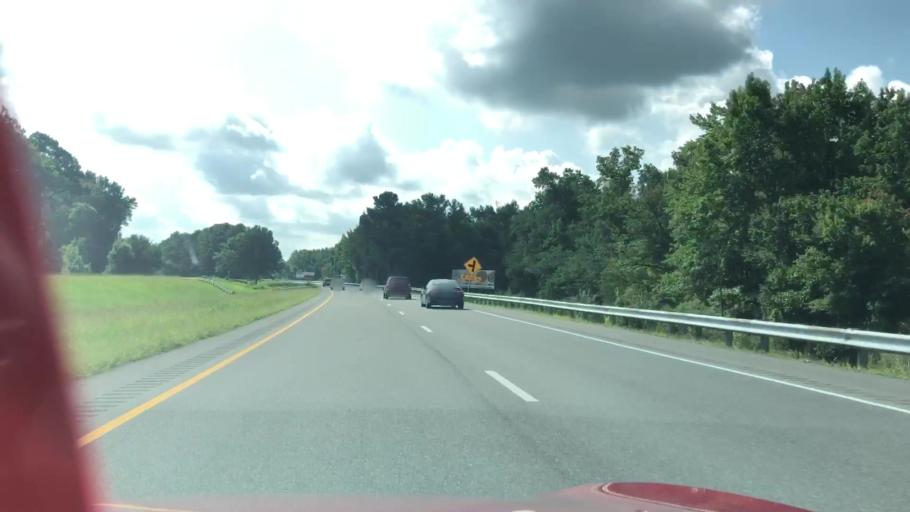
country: US
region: Maryland
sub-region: Somerset County
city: Princess Anne
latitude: 38.1348
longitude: -75.7007
